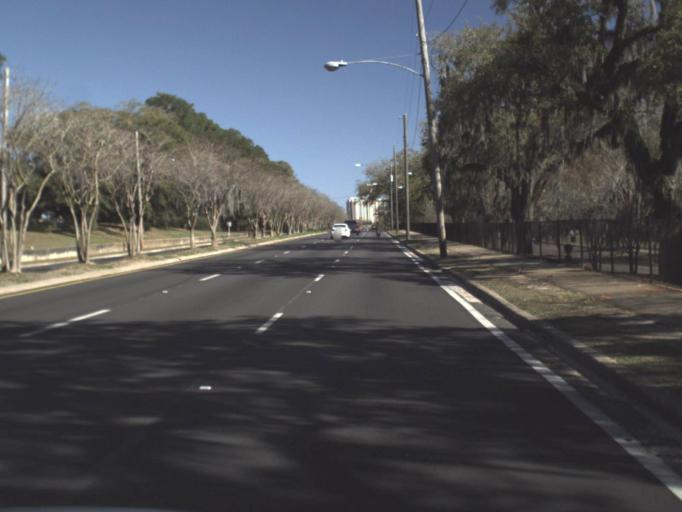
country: US
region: Florida
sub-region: Leon County
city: Tallahassee
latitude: 30.4479
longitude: -84.3017
